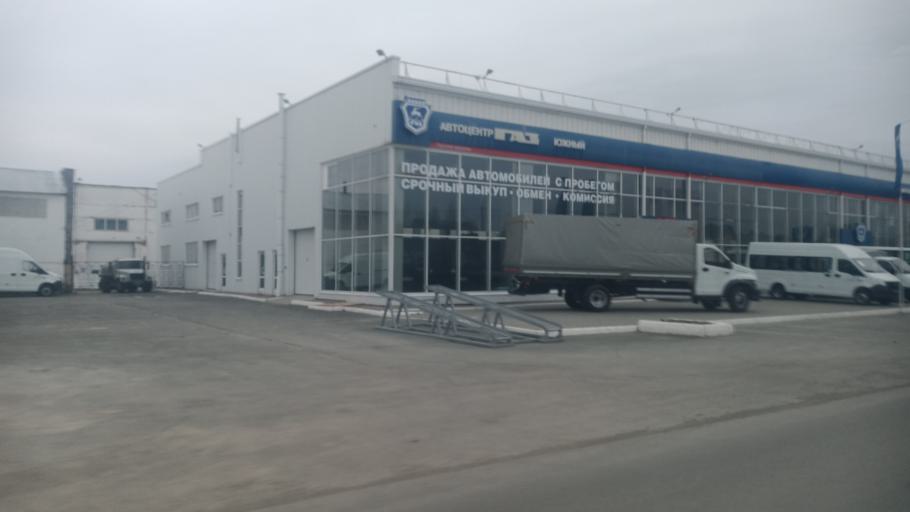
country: RU
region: Altai Krai
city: Yuzhnyy
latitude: 53.2481
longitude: 83.6928
